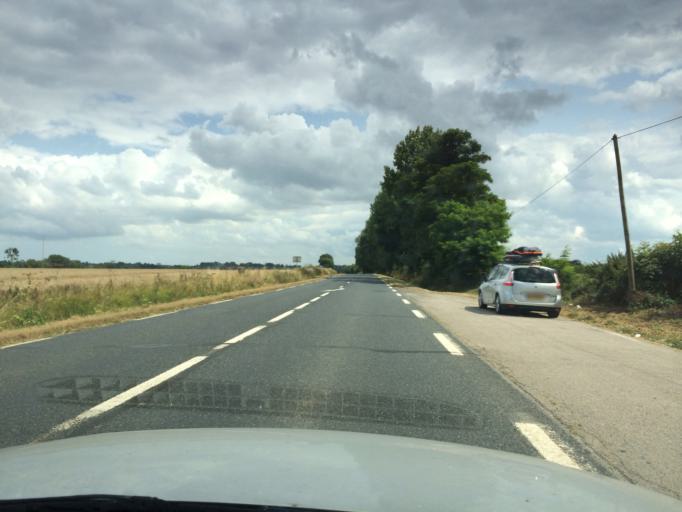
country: FR
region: Lower Normandy
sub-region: Departement du Calvados
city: Bayeux
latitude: 49.2890
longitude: -0.7541
